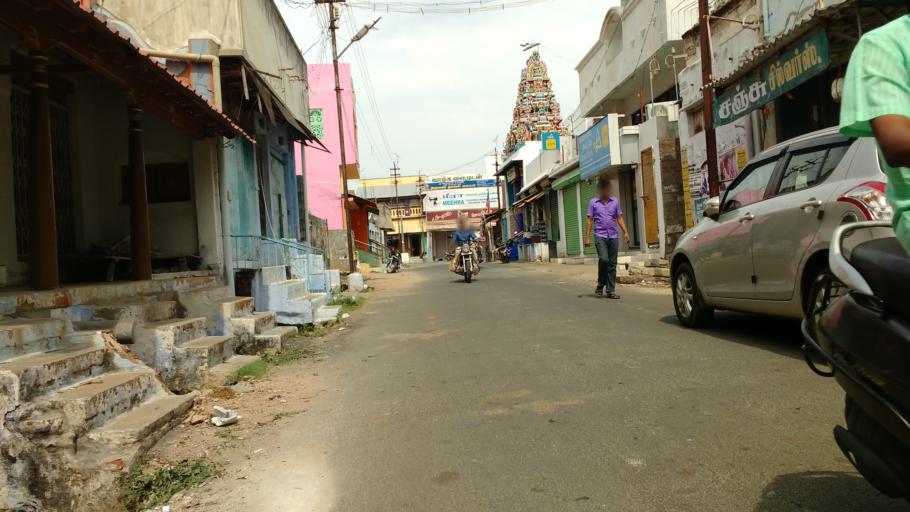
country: IN
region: Tamil Nadu
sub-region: Erode
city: Gobichettipalayam
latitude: 11.4571
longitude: 77.4348
